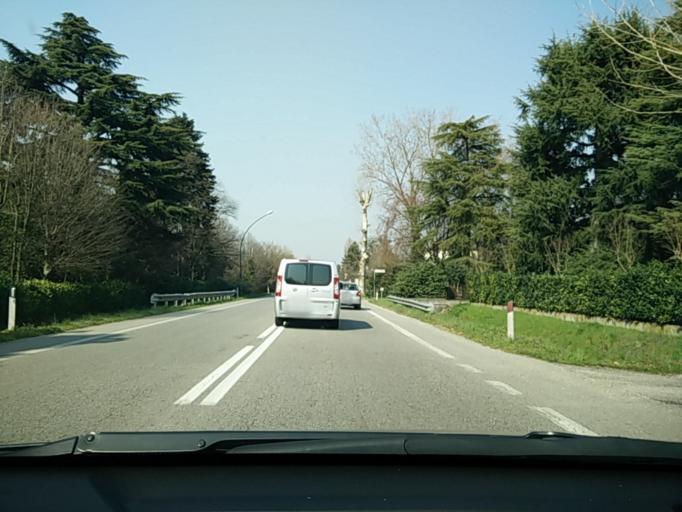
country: IT
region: Veneto
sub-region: Provincia di Treviso
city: Mogliano Veneto
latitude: 45.5438
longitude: 12.2362
